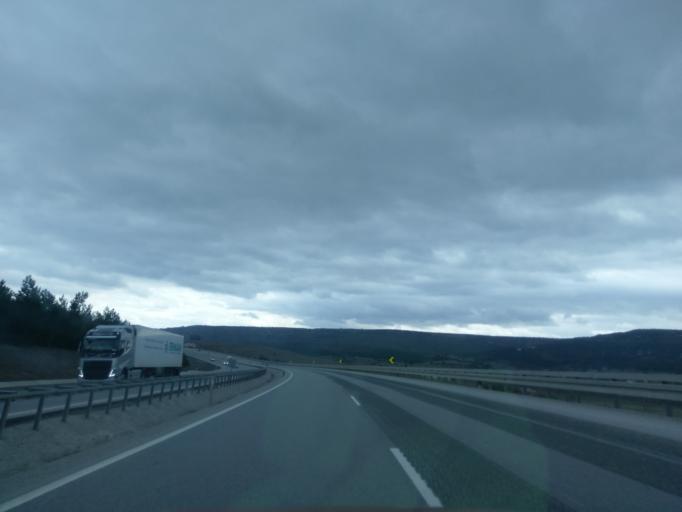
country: TR
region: Kuetahya
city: Sabuncu
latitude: 39.5718
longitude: 30.1047
